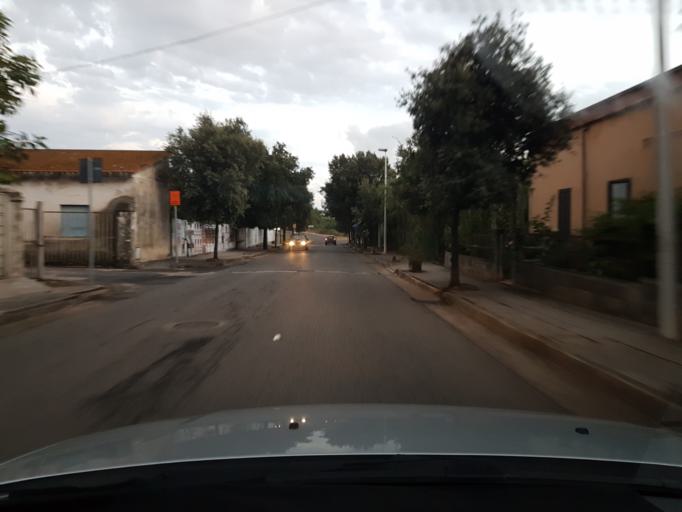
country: IT
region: Sardinia
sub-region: Provincia di Oristano
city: Tramatza
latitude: 39.9992
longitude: 8.6499
